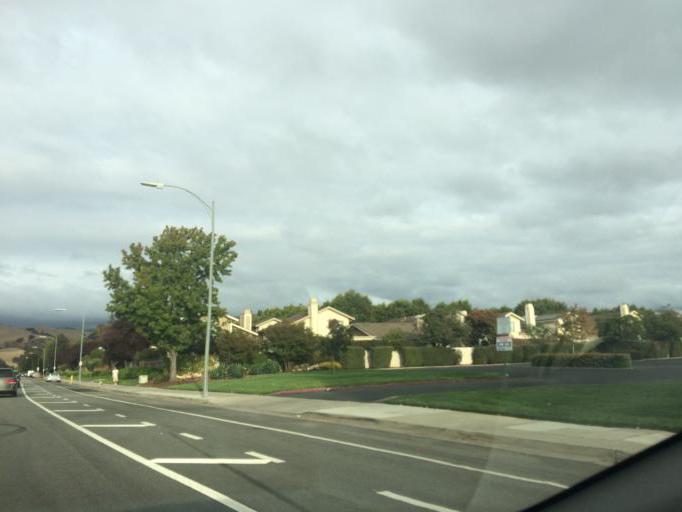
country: US
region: California
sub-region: Santa Clara County
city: Milpitas
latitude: 37.4096
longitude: -121.8692
